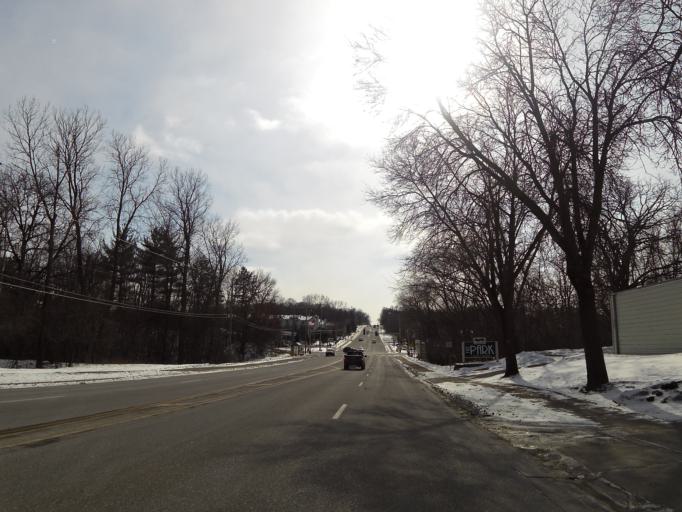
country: US
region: Minnesota
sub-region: Ramsey County
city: Maplewood
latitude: 44.9343
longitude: -93.0049
